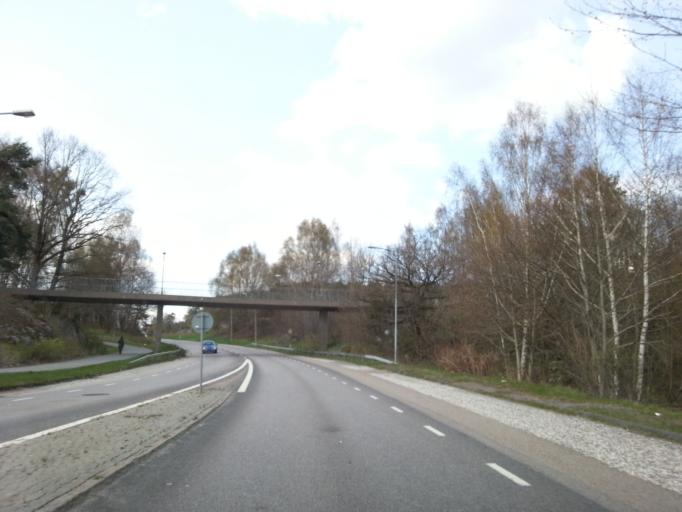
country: SE
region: Vaestra Goetaland
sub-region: Goteborg
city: Hammarkullen
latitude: 57.7729
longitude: 12.0235
